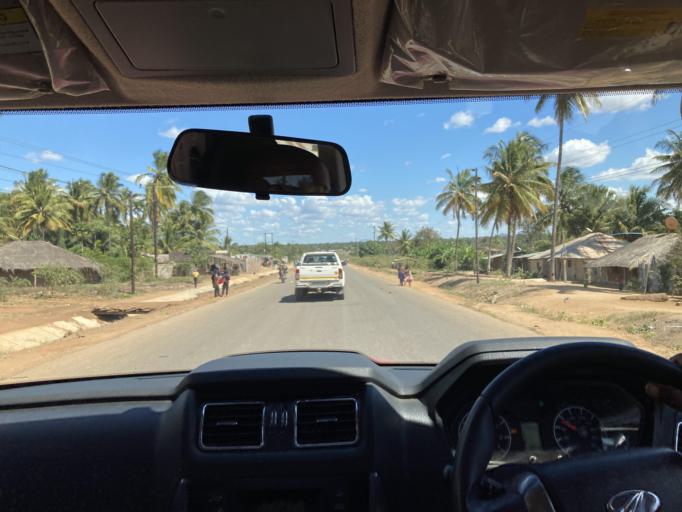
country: MZ
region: Cabo Delgado
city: Montepuez
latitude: -13.1335
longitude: 38.9919
